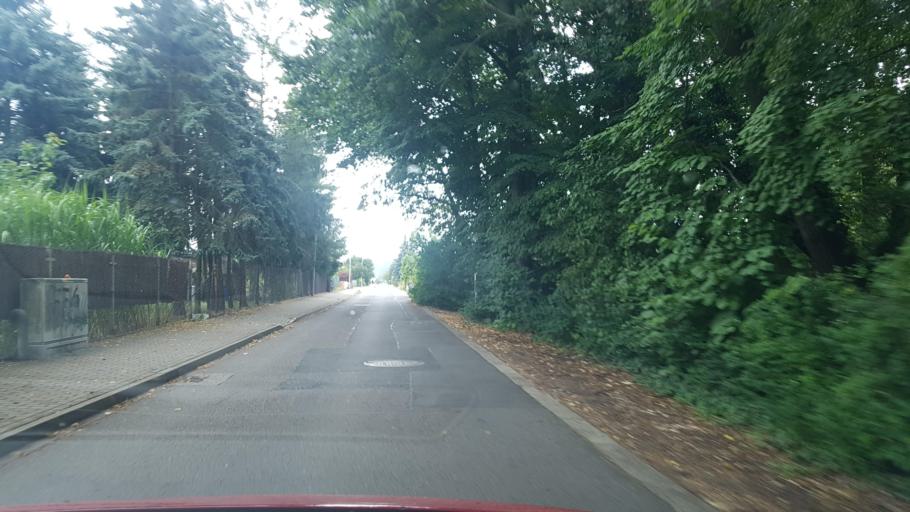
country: DE
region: Brandenburg
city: Herzberg
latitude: 51.6880
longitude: 13.2418
